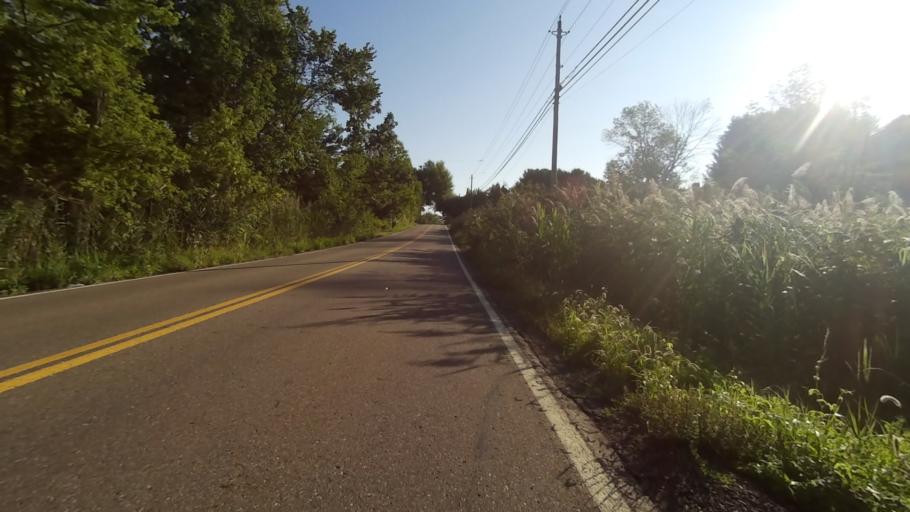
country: US
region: Ohio
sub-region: Portage County
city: Streetsboro
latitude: 41.2322
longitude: -81.3533
